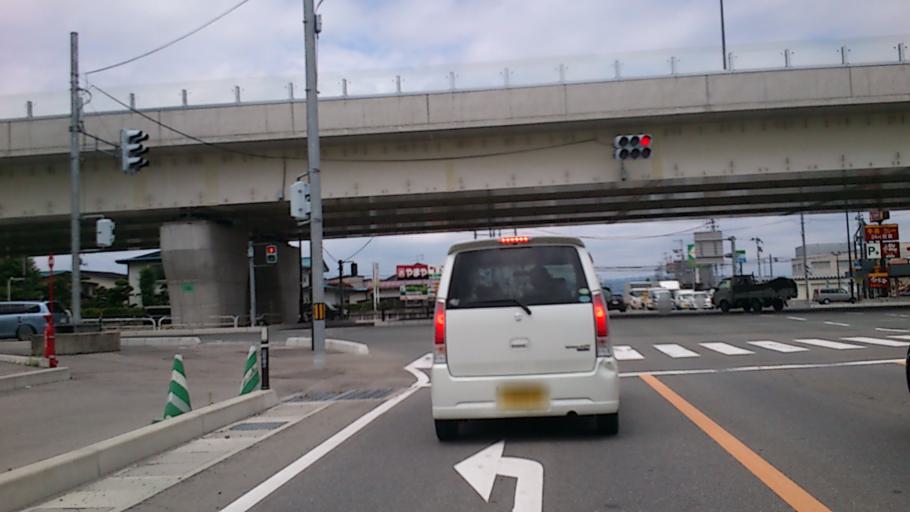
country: JP
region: Yamagata
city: Yamagata-shi
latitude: 38.2813
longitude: 140.3614
